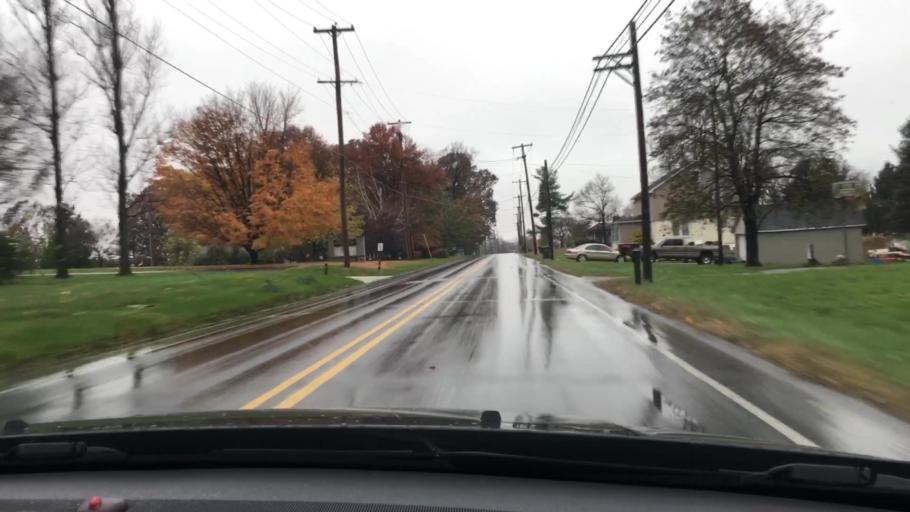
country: US
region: Pennsylvania
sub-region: York County
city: Susquehanna Trails
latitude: 39.8079
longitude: -76.3734
